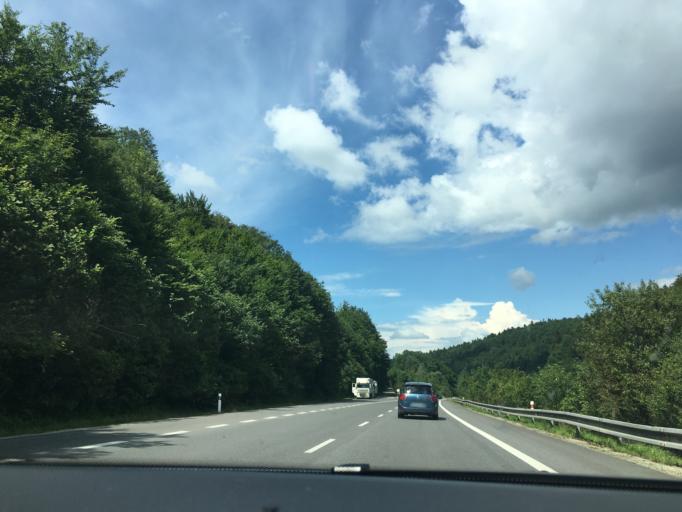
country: PL
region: Subcarpathian Voivodeship
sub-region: Powiat krosnienski
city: Jasliska
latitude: 49.3846
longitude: 21.6961
